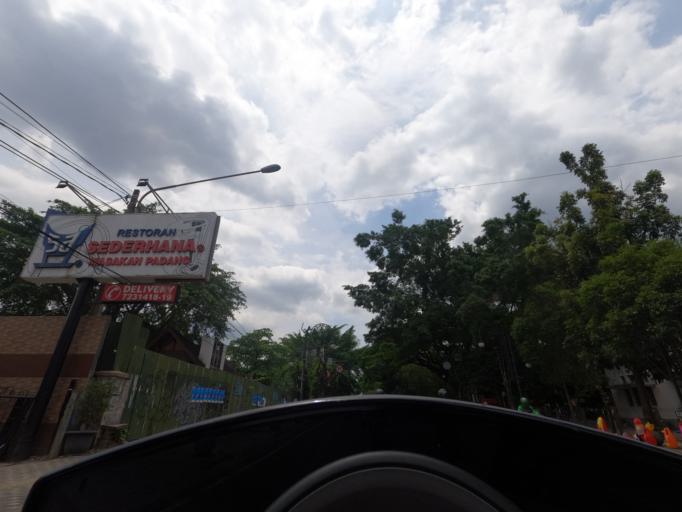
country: ID
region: West Java
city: Bandung
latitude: -6.9114
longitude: 107.6274
